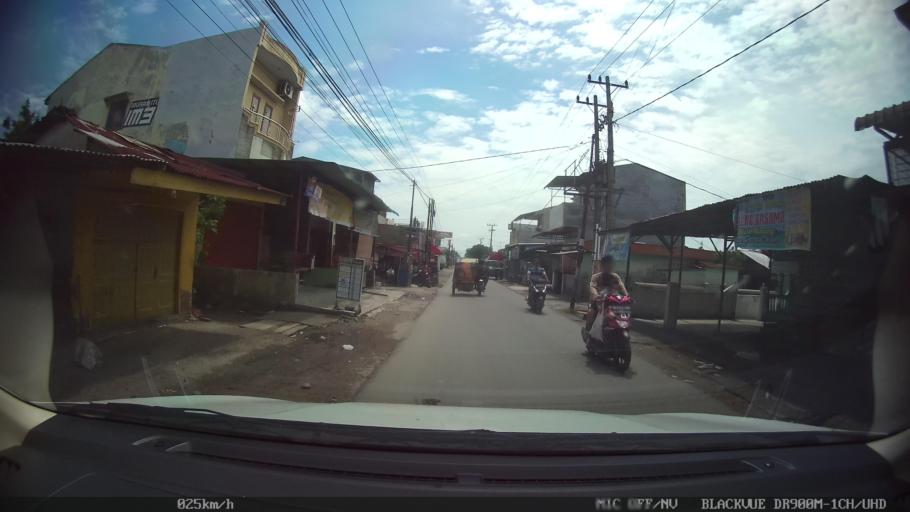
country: ID
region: North Sumatra
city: Medan
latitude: 3.5910
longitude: 98.7488
